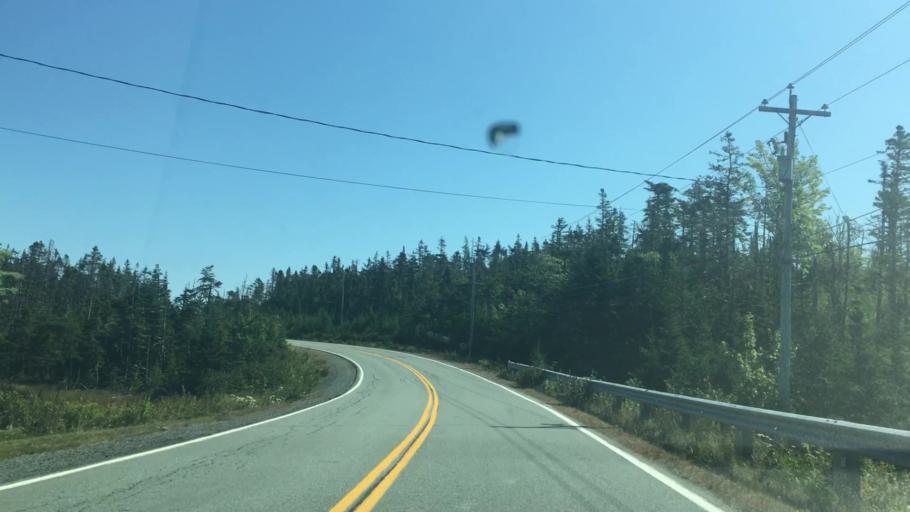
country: CA
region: Nova Scotia
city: Antigonish
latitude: 45.0069
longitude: -62.0880
